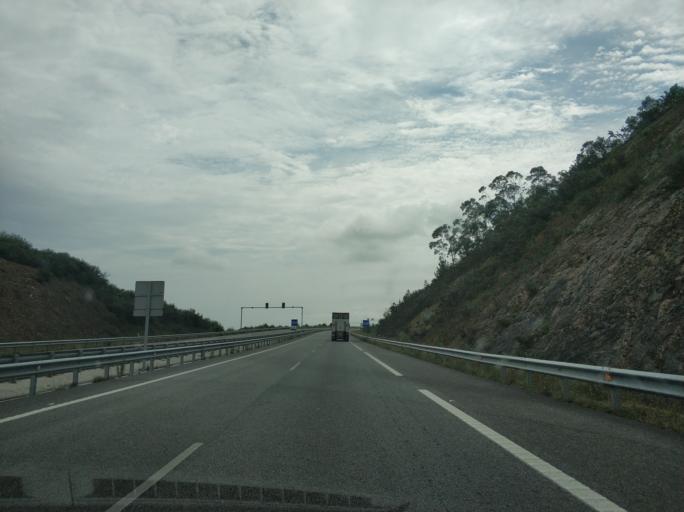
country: ES
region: Asturias
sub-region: Province of Asturias
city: Navia
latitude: 43.5351
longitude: -6.5958
